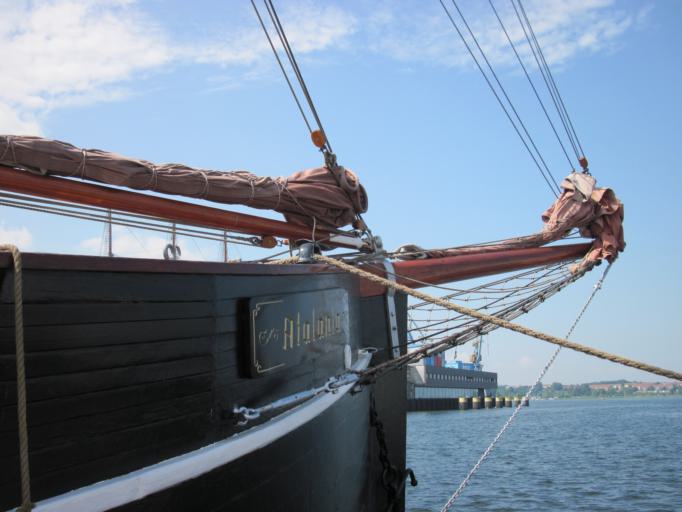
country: DE
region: Mecklenburg-Vorpommern
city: Wismar
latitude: 53.8993
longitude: 11.4569
